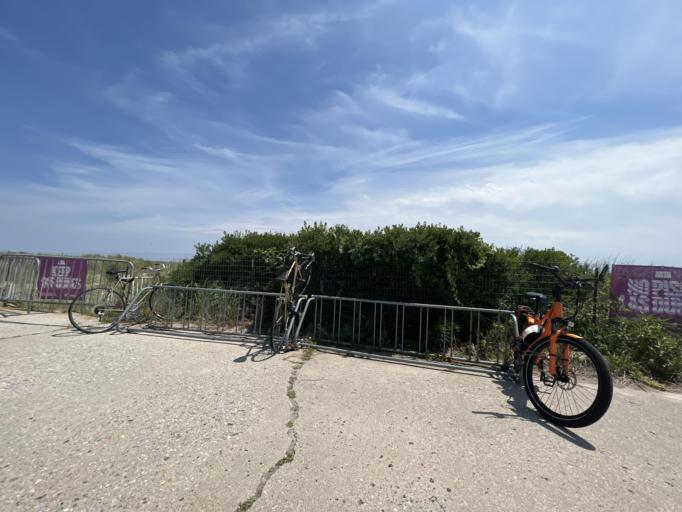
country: US
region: New York
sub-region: Kings County
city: East New York
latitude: 40.5617
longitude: -73.8833
